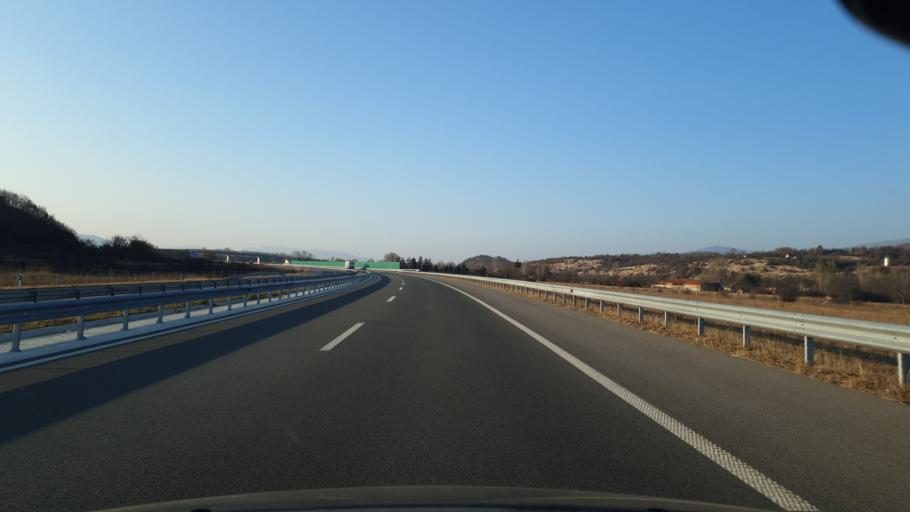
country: RS
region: Central Serbia
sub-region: Pirotski Okrug
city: Dimitrovgrad
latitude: 43.0555
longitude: 22.6963
